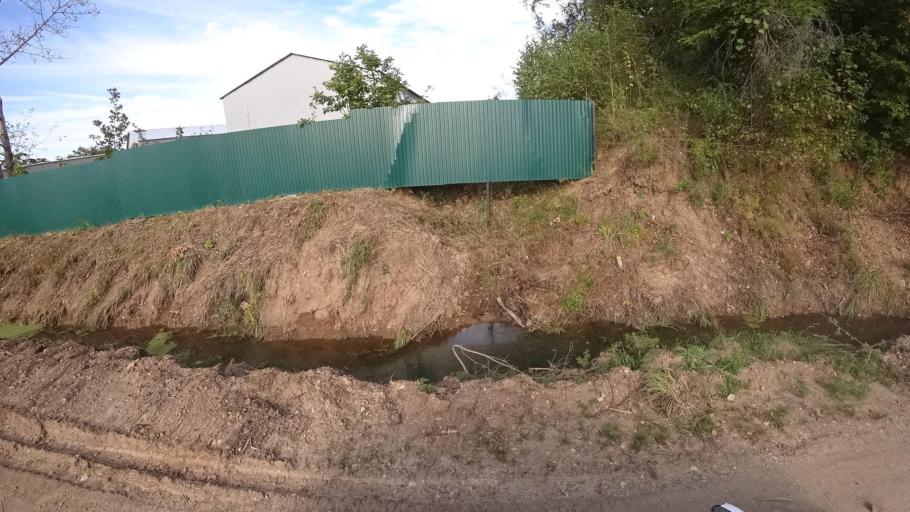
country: RU
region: Primorskiy
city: Dostoyevka
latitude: 44.3066
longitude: 133.4667
